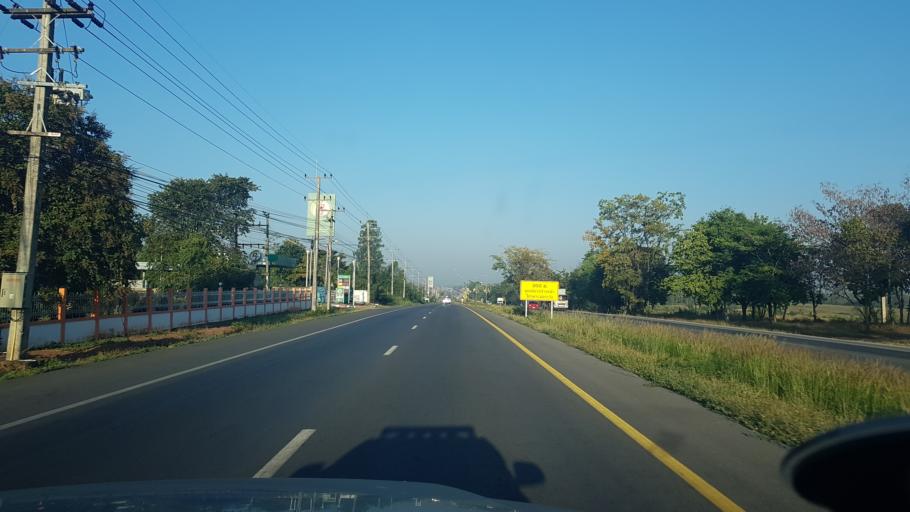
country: TH
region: Khon Kaen
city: Chum Phae
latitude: 16.5757
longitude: 102.0300
